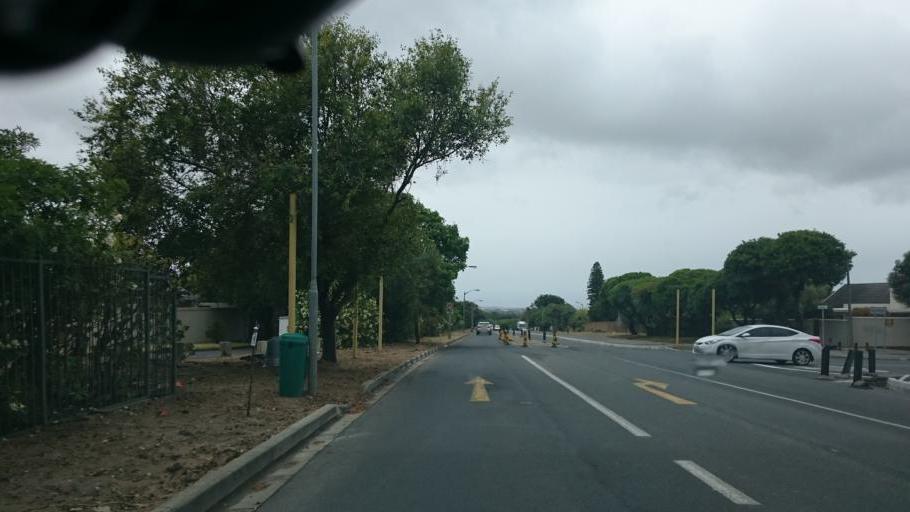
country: ZA
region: Western Cape
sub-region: City of Cape Town
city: Bergvliet
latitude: -34.0293
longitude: 18.4502
